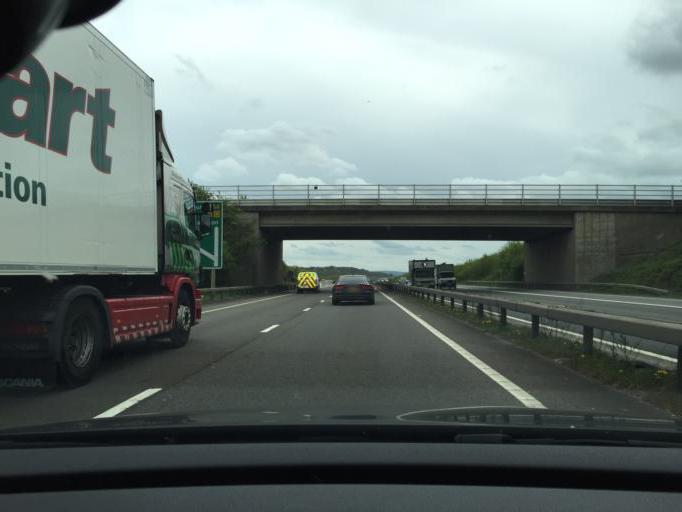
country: GB
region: England
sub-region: West Berkshire
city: Winterbourne
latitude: 51.4612
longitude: -1.3094
